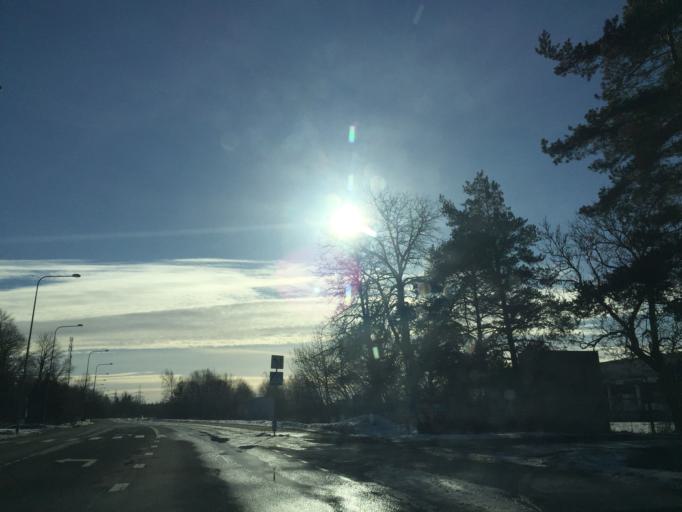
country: EE
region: Laeaene
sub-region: Lihula vald
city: Lihula
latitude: 58.5792
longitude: 23.5236
